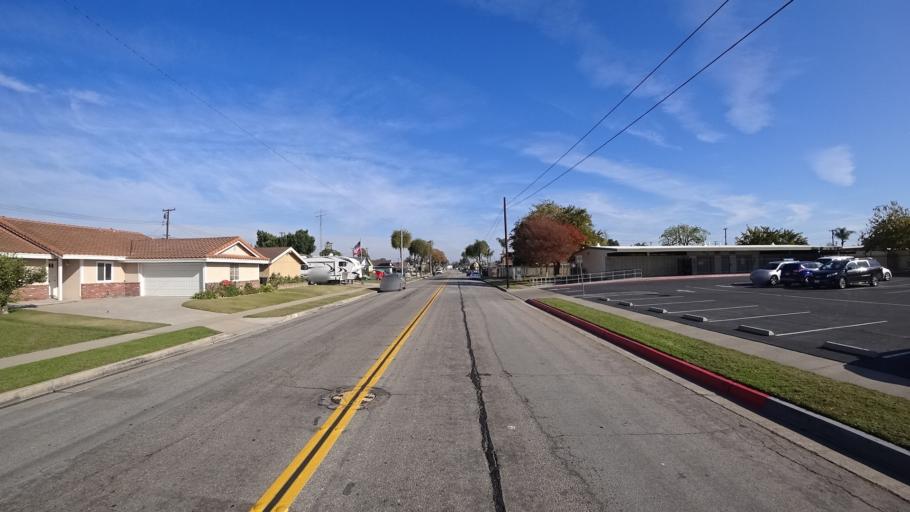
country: US
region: California
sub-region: Orange County
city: Westminster
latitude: 33.7777
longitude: -118.0184
